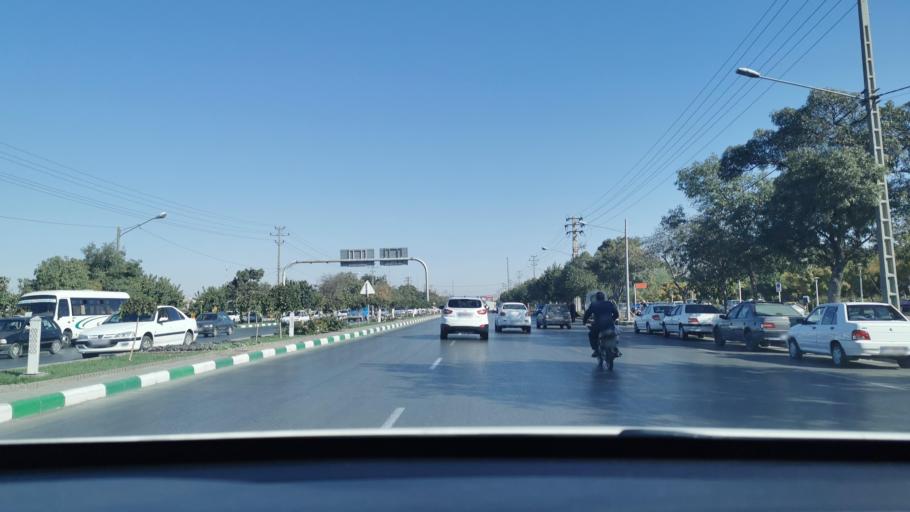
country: IR
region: Razavi Khorasan
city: Mashhad
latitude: 36.3322
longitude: 59.6251
